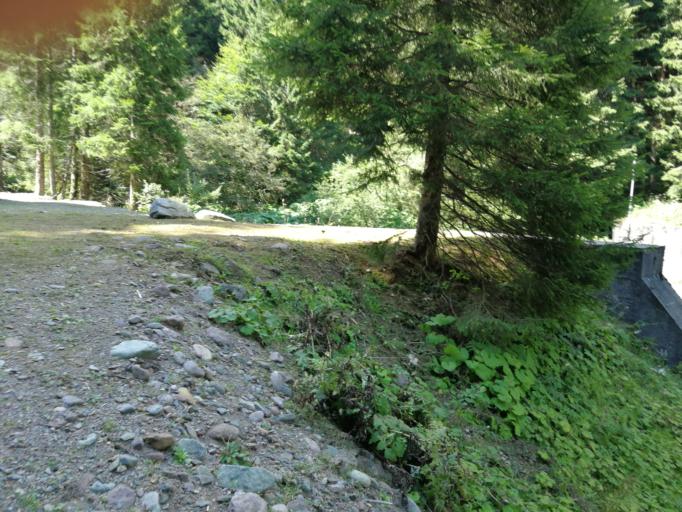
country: IT
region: Trentino-Alto Adige
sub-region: Provincia di Trento
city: Lodrone-Darzo
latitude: 45.8789
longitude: 10.5395
